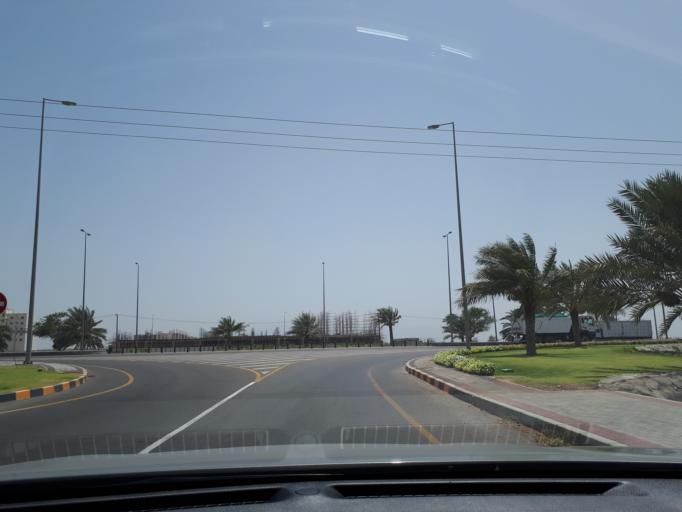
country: OM
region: Muhafazat Masqat
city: As Sib al Jadidah
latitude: 23.6848
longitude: 58.1038
